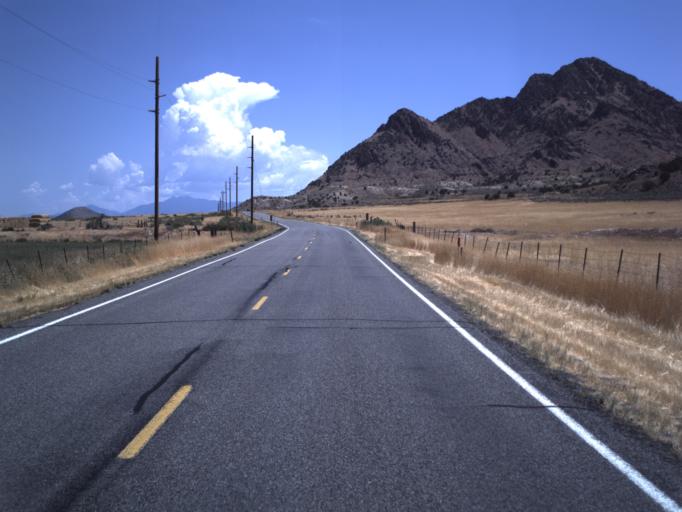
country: US
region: Utah
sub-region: Millard County
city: Delta
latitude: 39.5435
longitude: -112.2373
